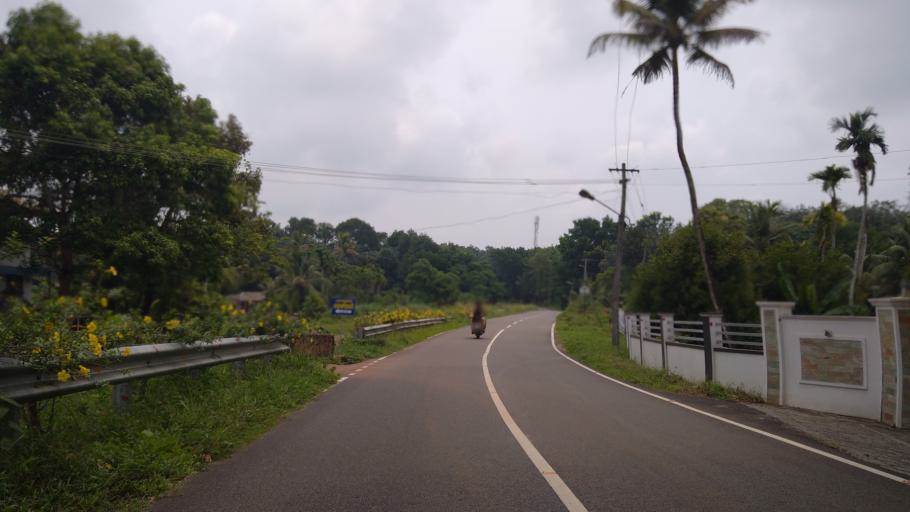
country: IN
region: Kerala
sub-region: Ernakulam
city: Ramamangalam
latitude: 10.0199
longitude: 76.4859
